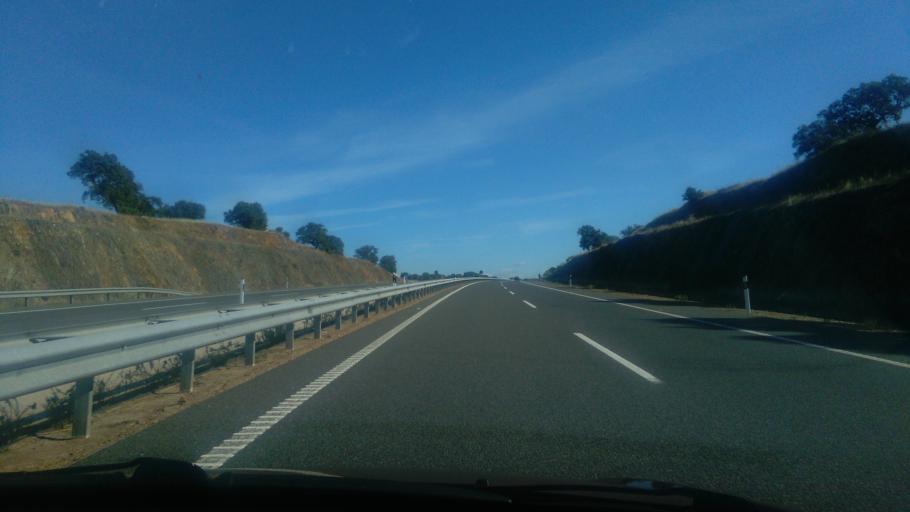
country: ES
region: Extremadura
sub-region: Provincia de Caceres
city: Plasenzuela
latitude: 39.4426
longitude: -6.0451
